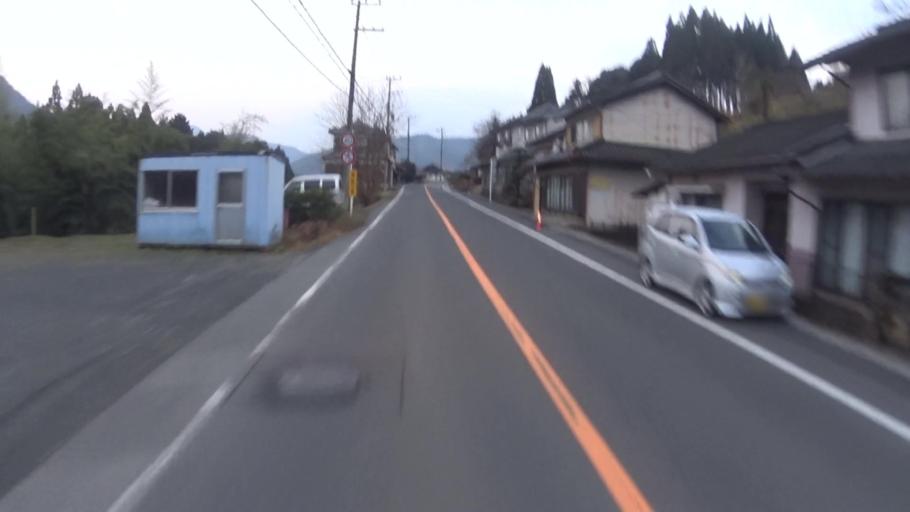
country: JP
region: Kyoto
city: Ayabe
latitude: 35.3014
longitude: 135.3140
